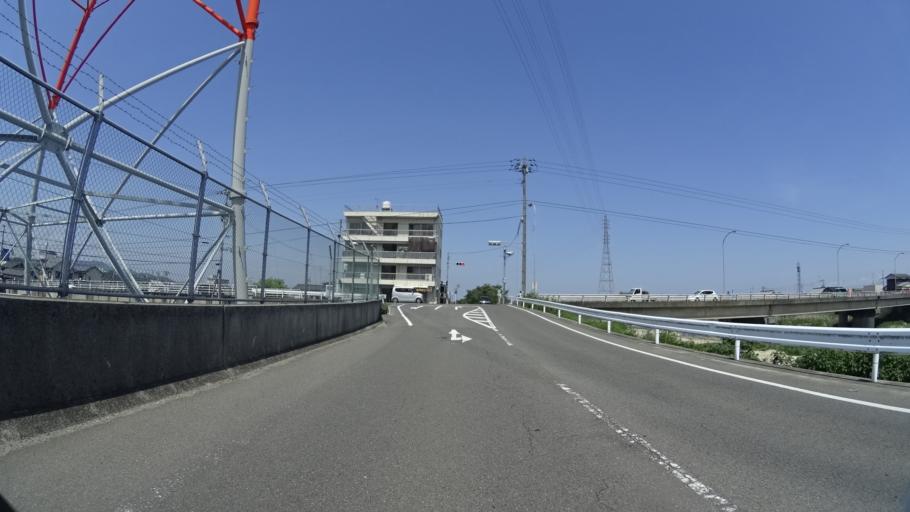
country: JP
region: Ehime
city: Hojo
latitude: 34.0388
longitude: 132.9767
